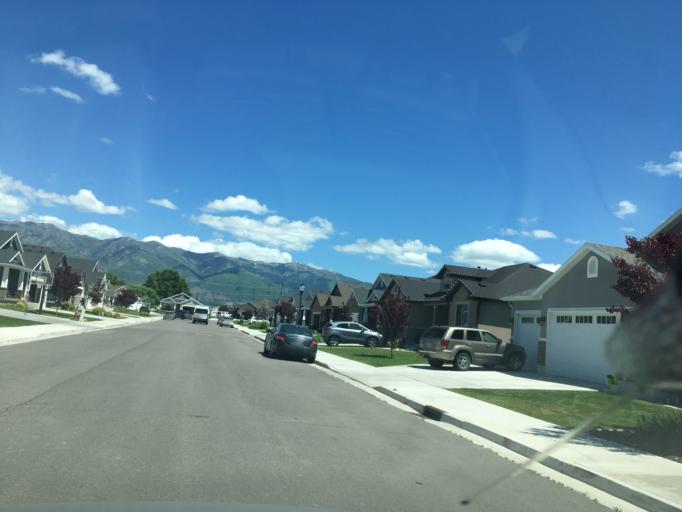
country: US
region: Utah
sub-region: Davis County
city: Layton
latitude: 41.0525
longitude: -112.0107
